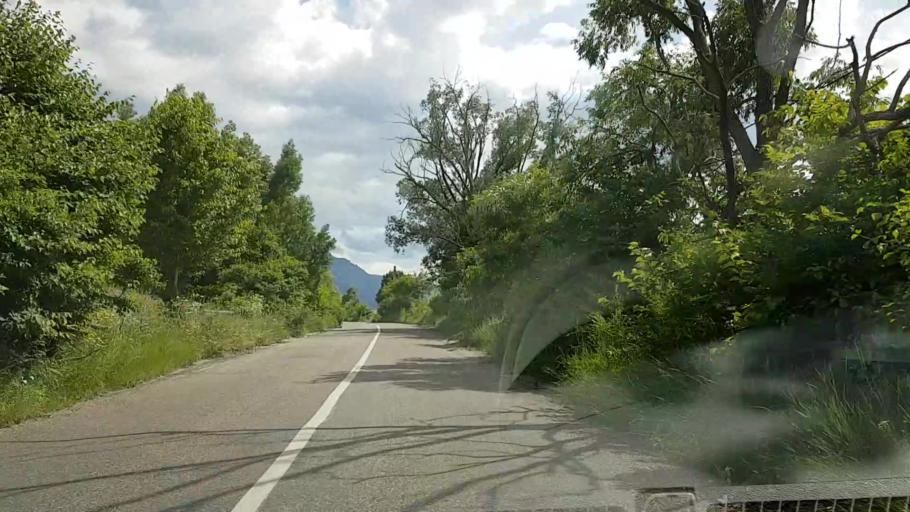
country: RO
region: Neamt
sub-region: Comuna Ceahlau
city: Ceahlau
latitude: 47.0700
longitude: 25.9609
